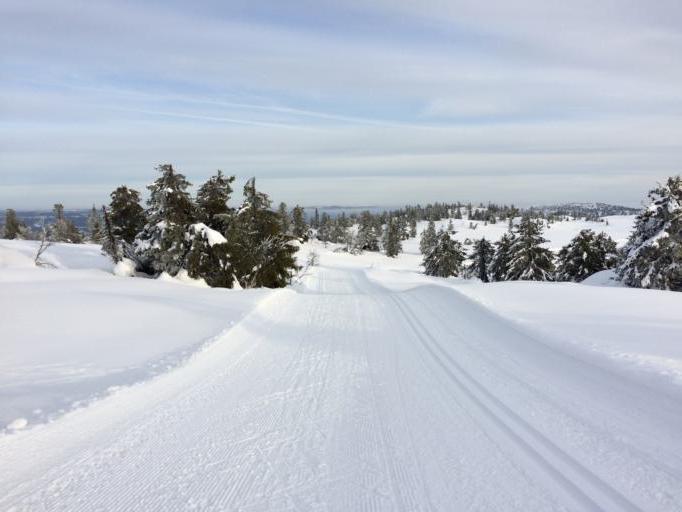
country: NO
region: Oppland
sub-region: Gausdal
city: Segalstad bru
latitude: 61.3271
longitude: 10.0361
